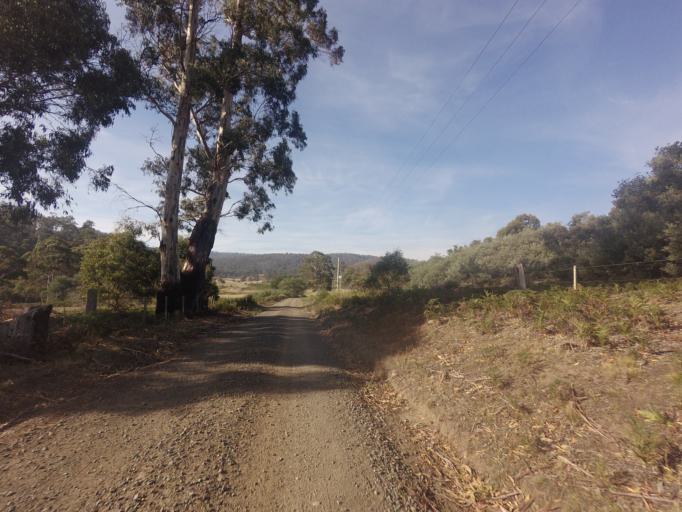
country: AU
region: Tasmania
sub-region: Sorell
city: Sorell
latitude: -42.5319
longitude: 147.4389
